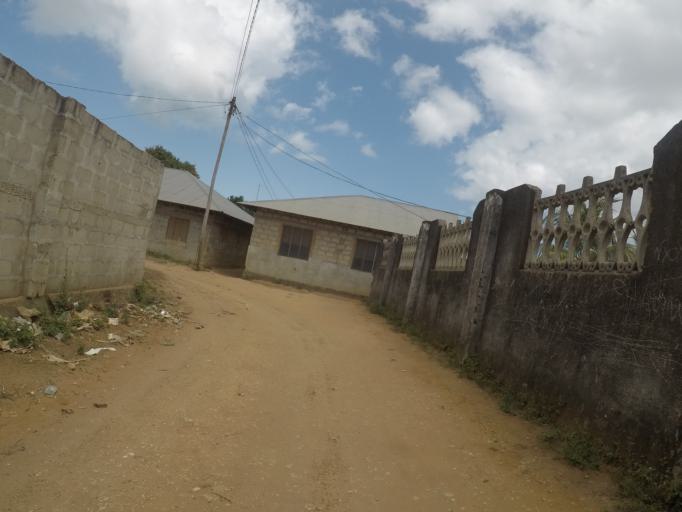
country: TZ
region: Zanzibar Urban/West
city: Zanzibar
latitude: -6.2035
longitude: 39.2305
